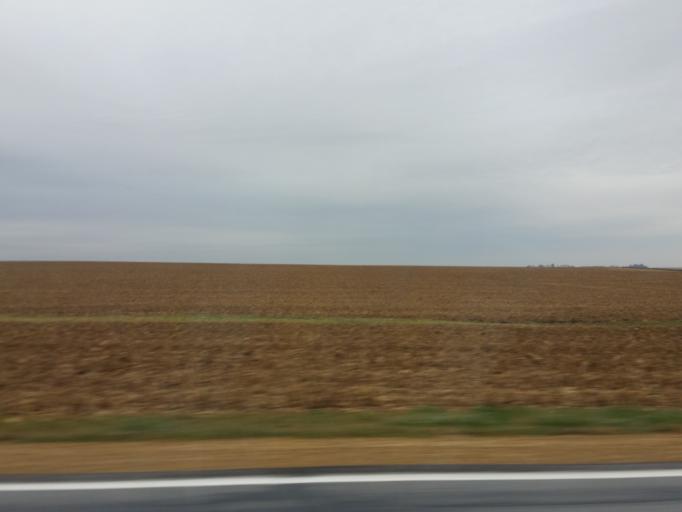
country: US
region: Iowa
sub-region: Black Hawk County
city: La Porte City
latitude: 42.2307
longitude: -92.2010
